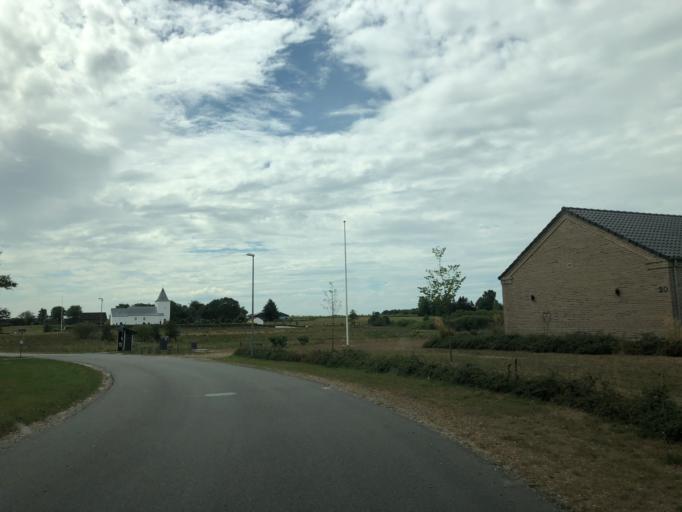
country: DK
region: South Denmark
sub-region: Billund Kommune
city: Grindsted
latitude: 55.6486
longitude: 8.8089
